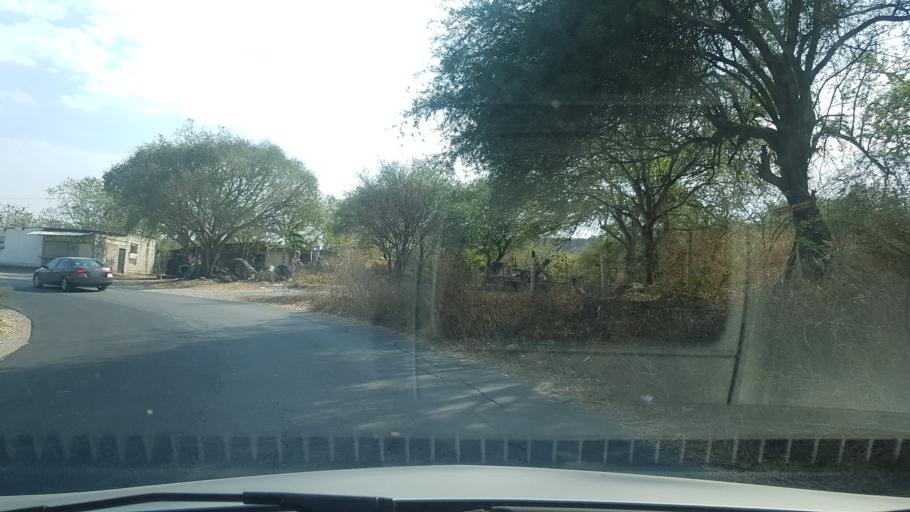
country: MX
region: Morelos
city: Ahuehuetzingo
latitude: 18.6482
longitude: -99.3019
